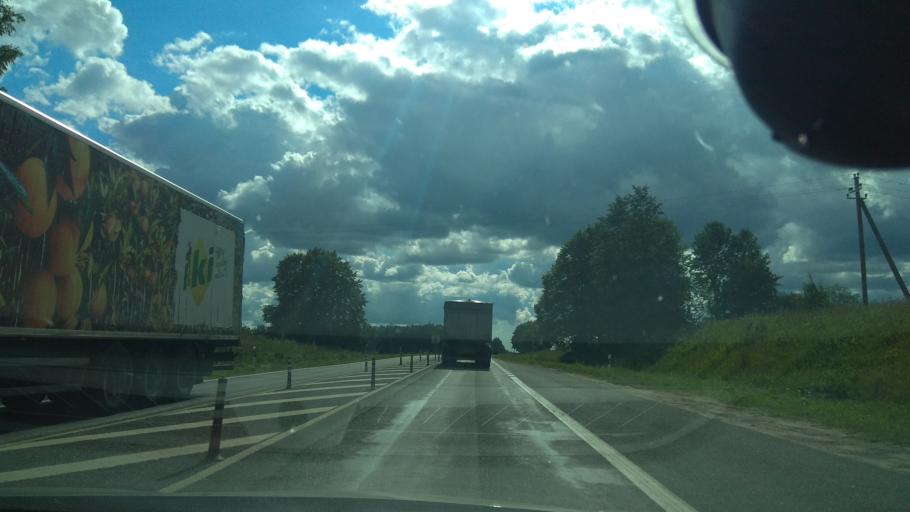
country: LT
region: Telsiu apskritis
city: Plunge
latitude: 55.9504
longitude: 21.9426
